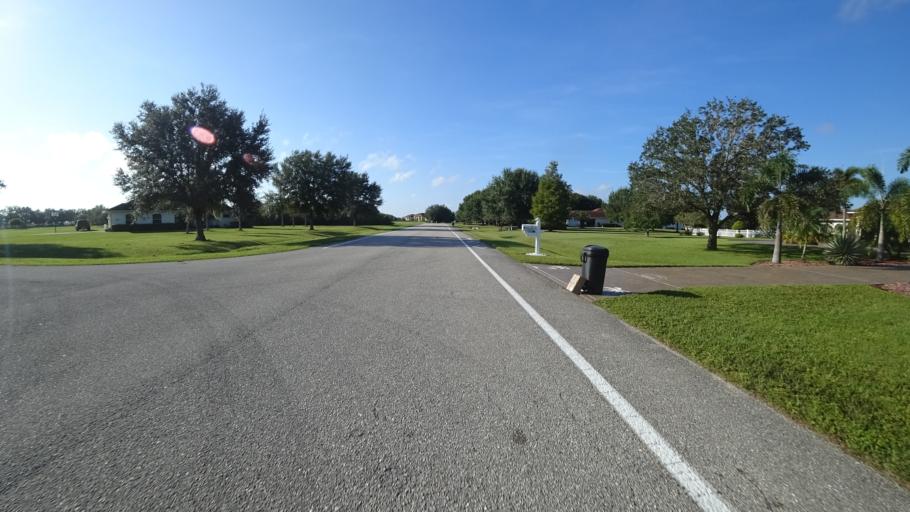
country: US
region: Florida
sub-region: Hillsborough County
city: Sun City Center
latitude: 27.5552
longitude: -82.3536
